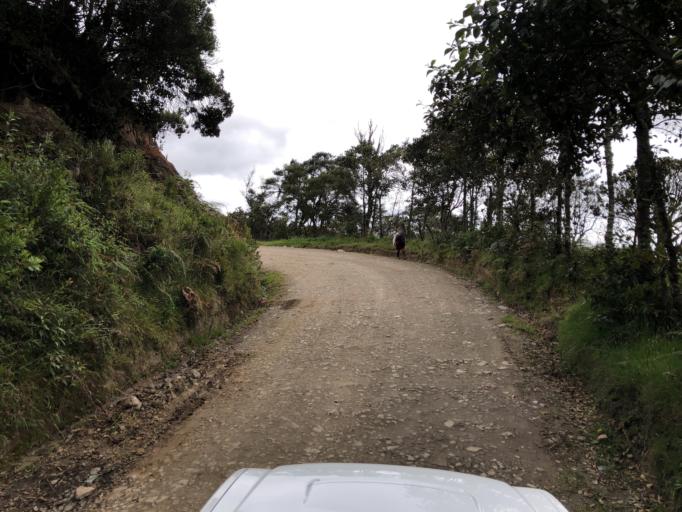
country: CO
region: Cauca
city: Totoro
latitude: 2.5062
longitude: -76.3624
